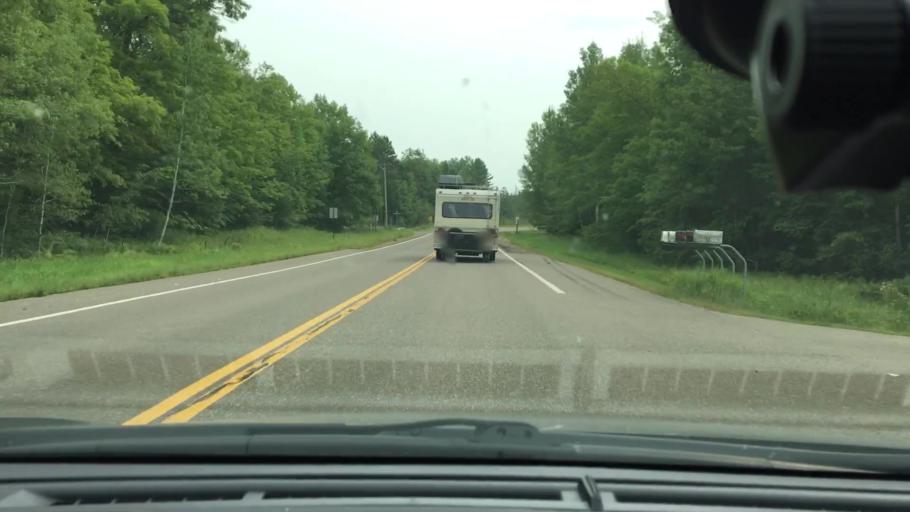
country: US
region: Minnesota
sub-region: Aitkin County
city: Aitkin
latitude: 46.4071
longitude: -93.8117
